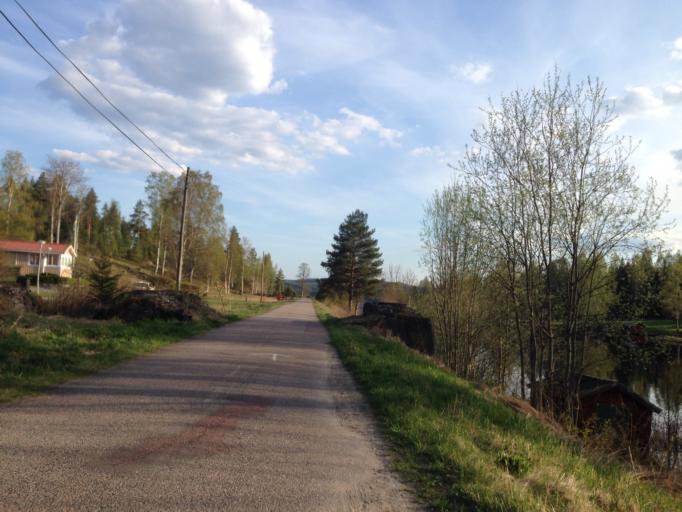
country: SE
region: Dalarna
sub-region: Ludvika Kommun
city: Ludvika
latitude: 60.1683
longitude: 15.1627
